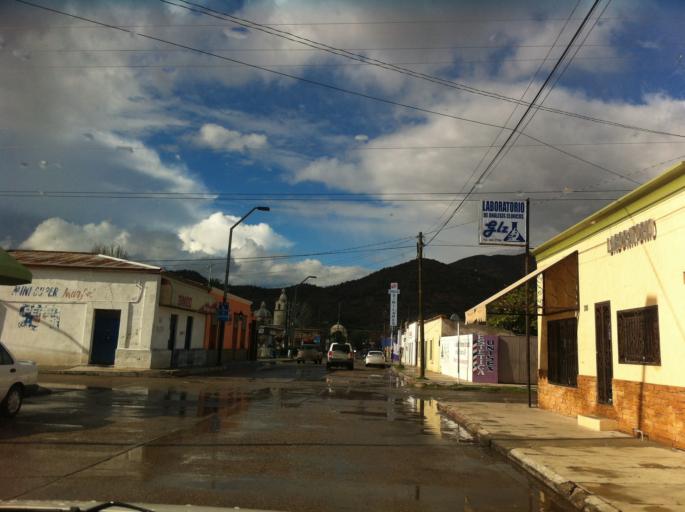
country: MX
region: Sonora
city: Magdalena de Kino
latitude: 30.6284
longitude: -110.9713
